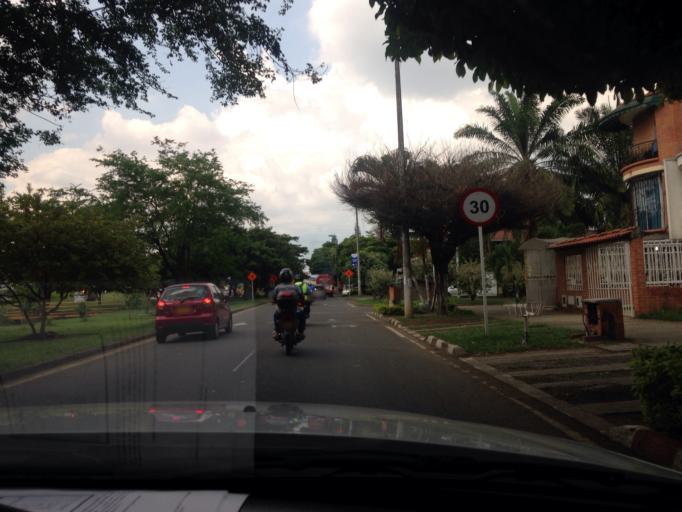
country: CO
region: Valle del Cauca
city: Cali
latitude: 3.3867
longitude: -76.5162
